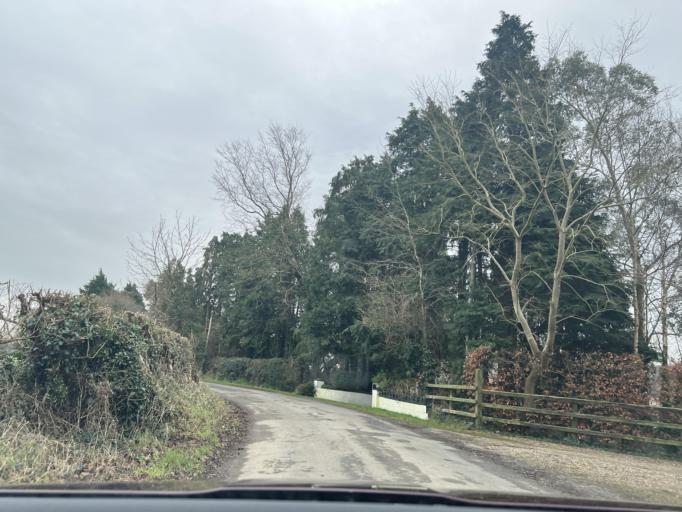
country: IE
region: Leinster
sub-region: Loch Garman
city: Castlebridge
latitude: 52.3867
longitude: -6.5298
